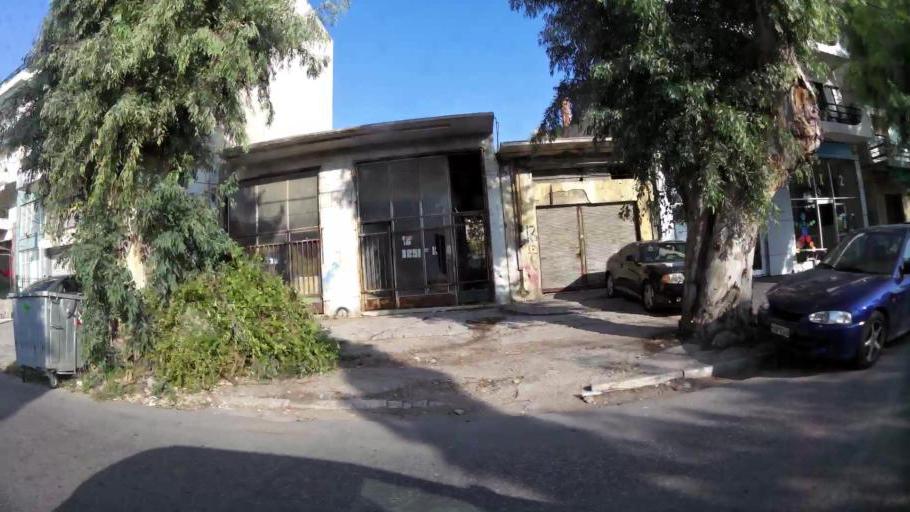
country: GR
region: Attica
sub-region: Nomarchia Anatolikis Attikis
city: Acharnes
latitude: 38.0760
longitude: 23.7345
